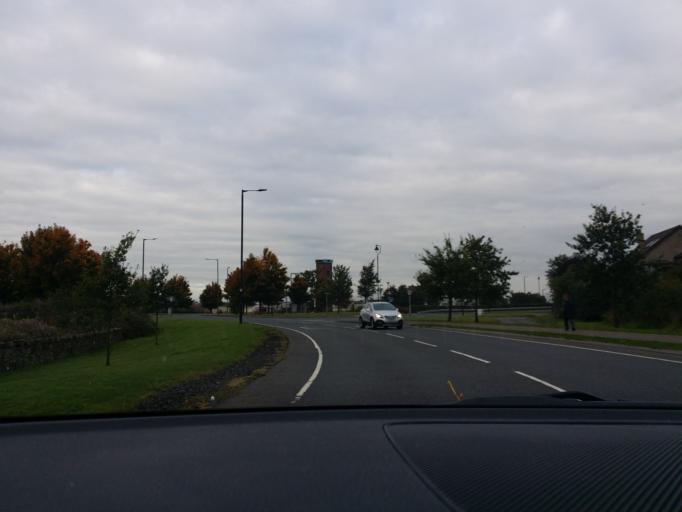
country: GB
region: Scotland
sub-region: Stirling
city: Stirling
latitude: 56.1242
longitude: -3.9530
